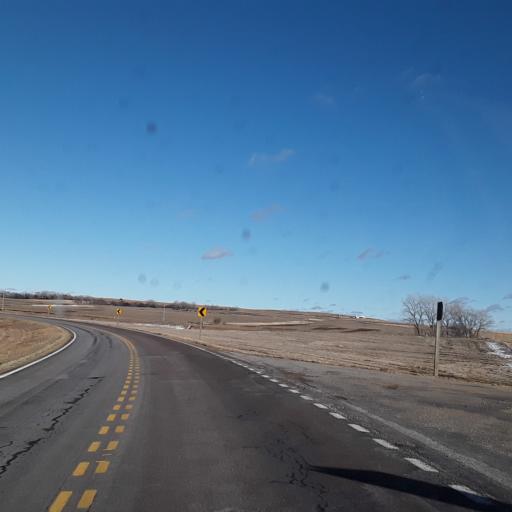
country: US
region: Kansas
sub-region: Cloud County
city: Concordia
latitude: 39.4964
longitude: -97.7263
